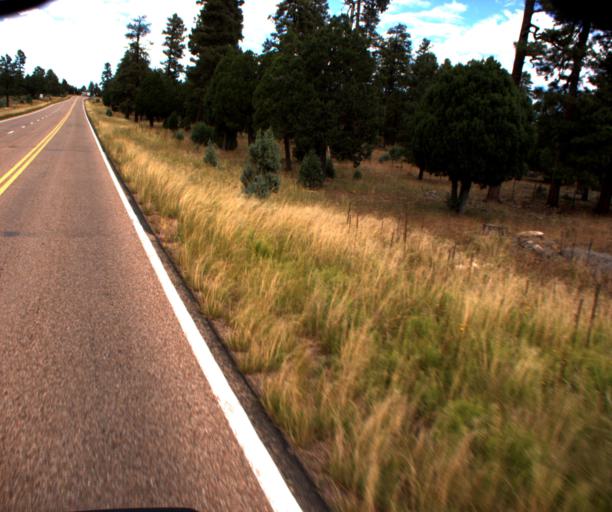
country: US
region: Arizona
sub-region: Navajo County
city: Heber-Overgaard
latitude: 34.3886
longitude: -110.6710
